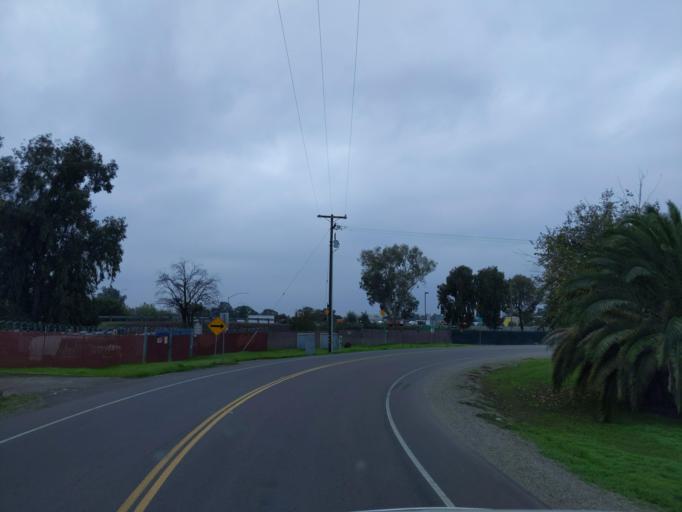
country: US
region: California
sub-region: San Joaquin County
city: Garden Acres
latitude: 37.9716
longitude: -121.2441
